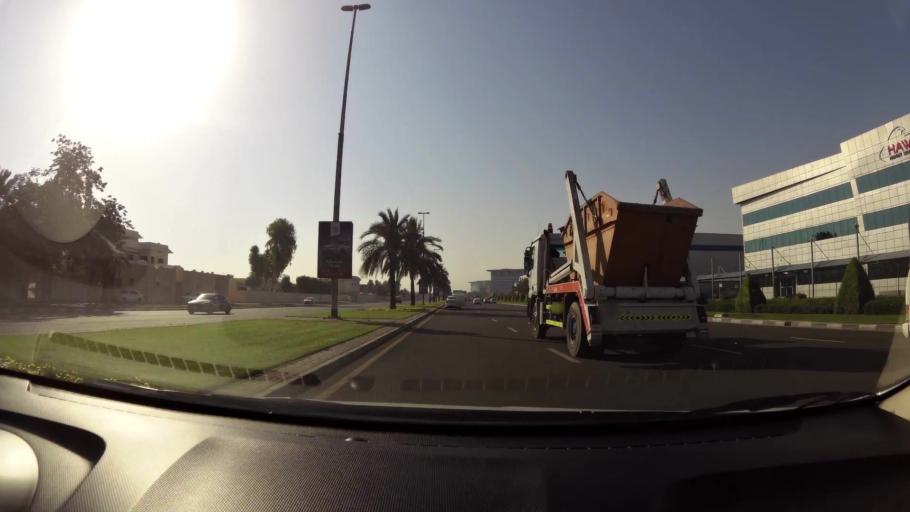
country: AE
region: Ash Shariqah
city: Sharjah
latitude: 25.2657
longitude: 55.3677
